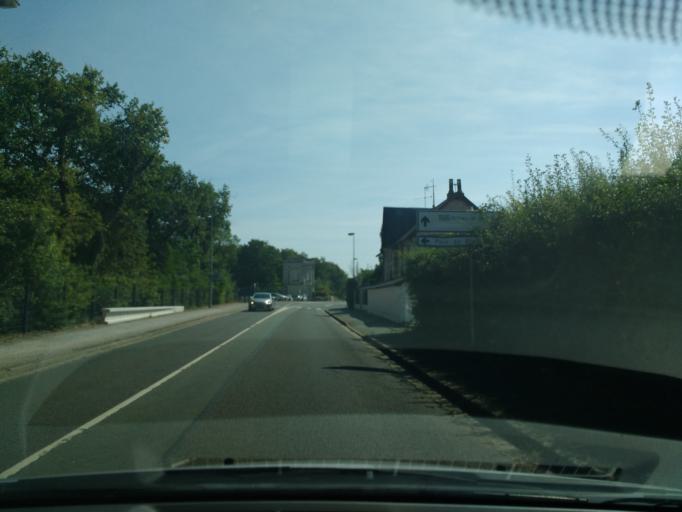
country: FR
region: Pays de la Loire
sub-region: Departement de Maine-et-Loire
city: Trelaze
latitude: 47.4669
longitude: -0.4845
